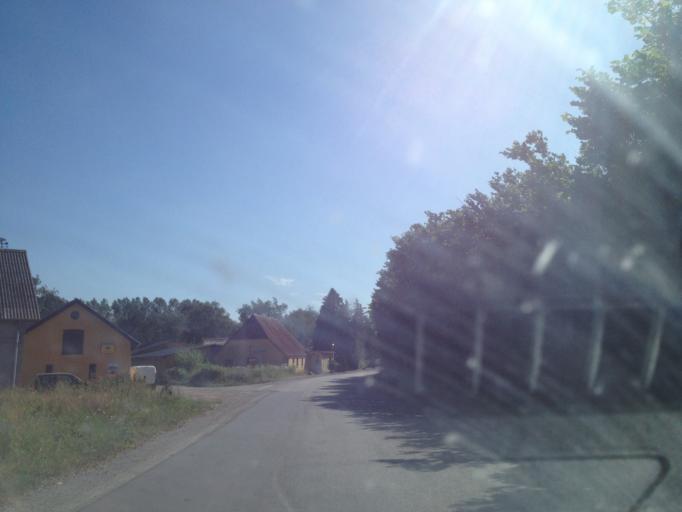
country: DK
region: South Denmark
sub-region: Kolding Kommune
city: Christiansfeld
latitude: 55.4044
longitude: 9.4983
